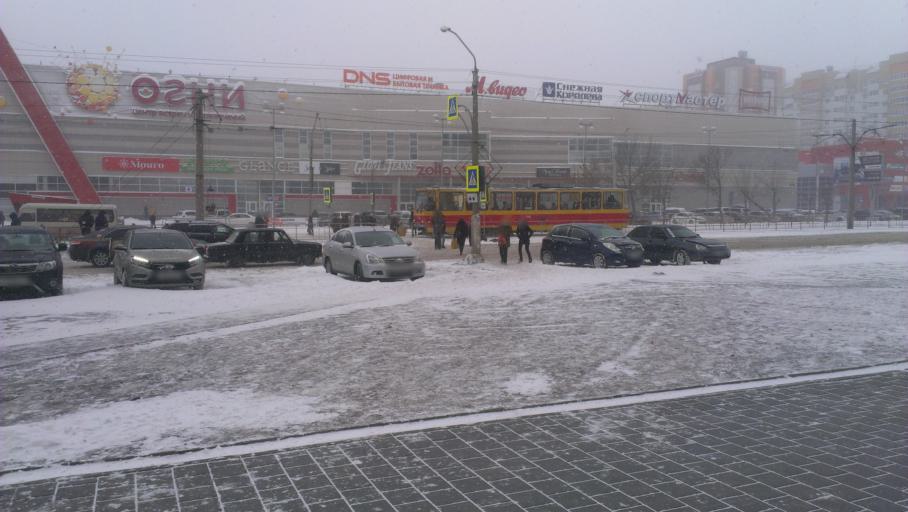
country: RU
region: Altai Krai
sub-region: Gorod Barnaulskiy
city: Barnaul
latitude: 53.3601
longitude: 83.6985
